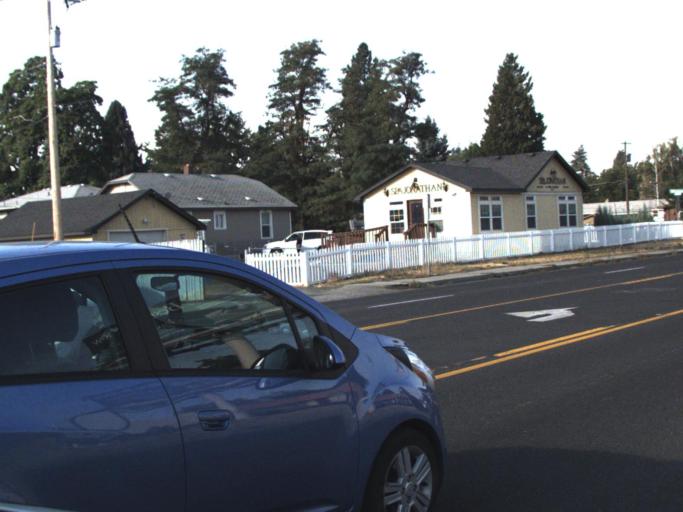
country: US
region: Washington
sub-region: Spokane County
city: Town and Country
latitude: 47.7151
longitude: -117.4158
